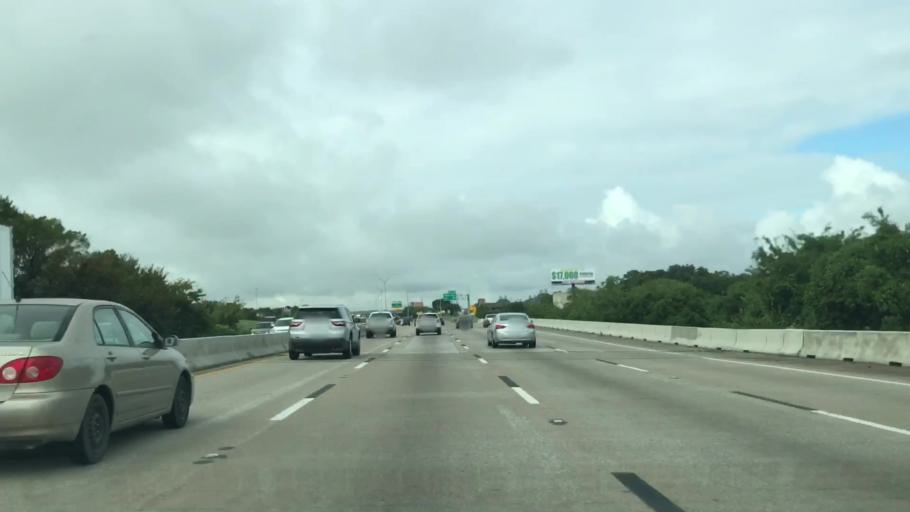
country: US
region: Texas
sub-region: Dallas County
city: Rowlett
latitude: 32.8681
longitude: -96.5378
